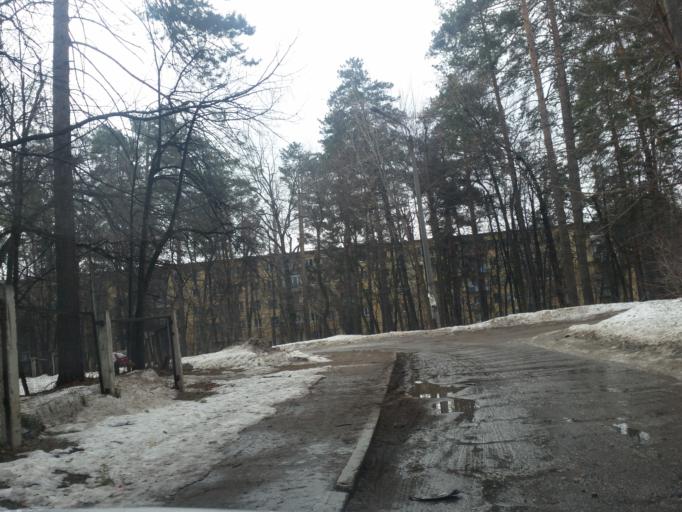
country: RU
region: Ulyanovsk
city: Dimitrovgrad
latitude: 54.2362
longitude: 49.5550
